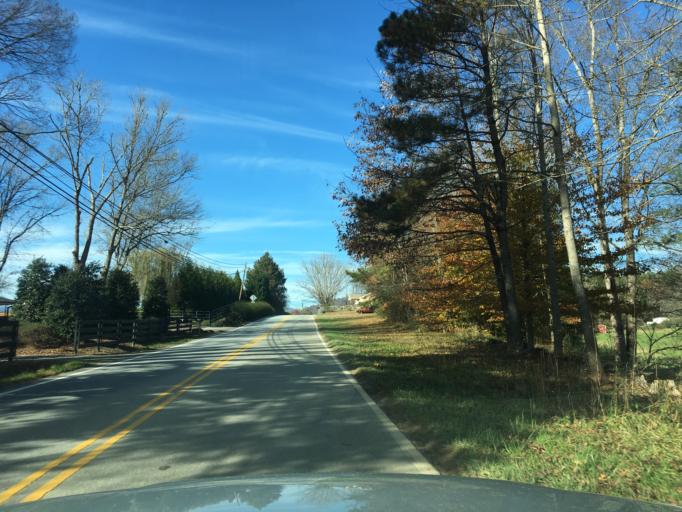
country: US
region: North Carolina
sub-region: Henderson County
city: Etowah
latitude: 35.2498
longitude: -82.6319
